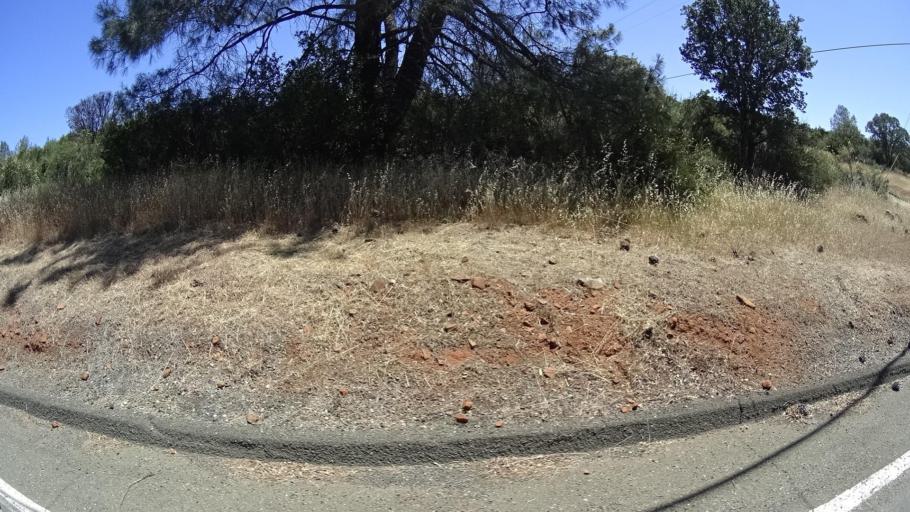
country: US
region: California
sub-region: Lake County
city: Hidden Valley Lake
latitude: 38.8215
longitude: -122.5473
